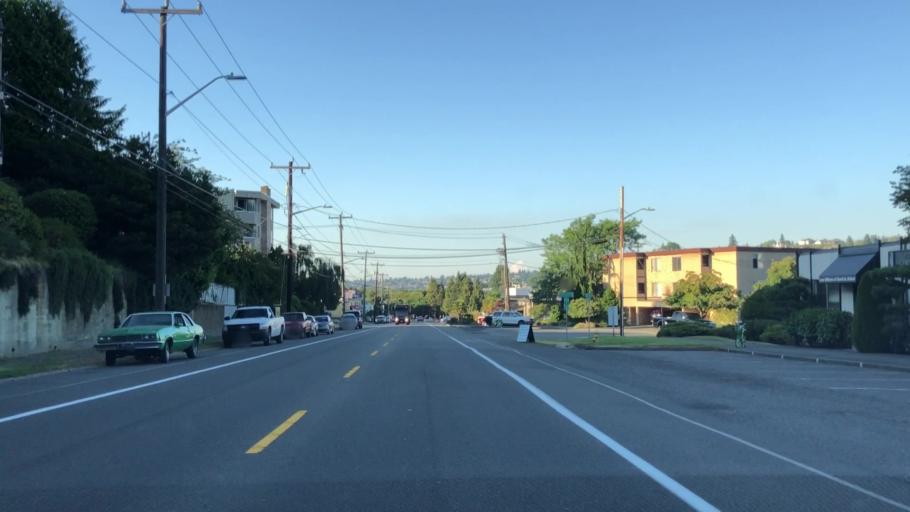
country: US
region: Washington
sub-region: King County
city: Seattle
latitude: 47.6437
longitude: -122.3840
